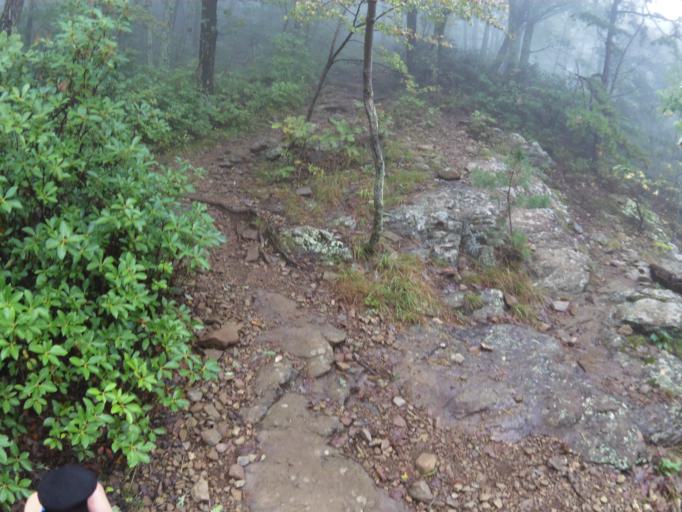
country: US
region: Virginia
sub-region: Rappahannock County
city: Washington
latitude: 38.7827
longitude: -78.2931
